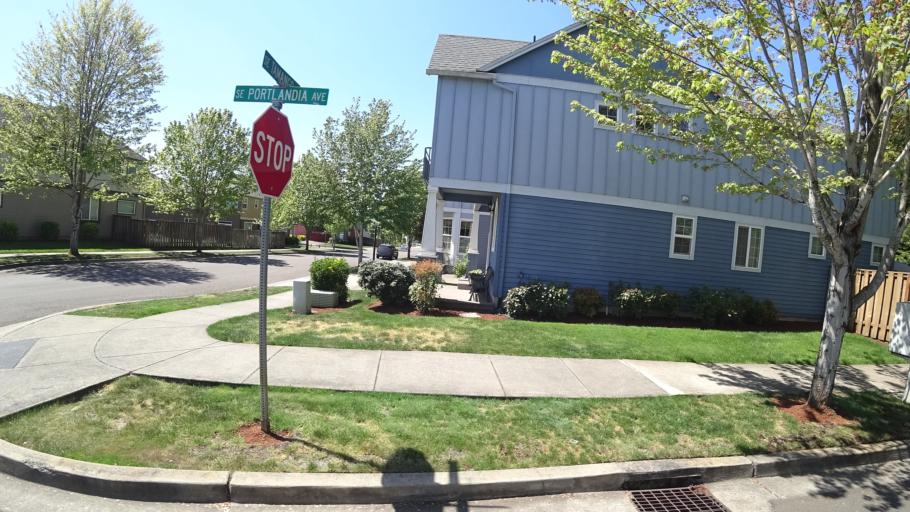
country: US
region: Oregon
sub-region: Washington County
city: Hillsboro
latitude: 45.5099
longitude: -122.9755
